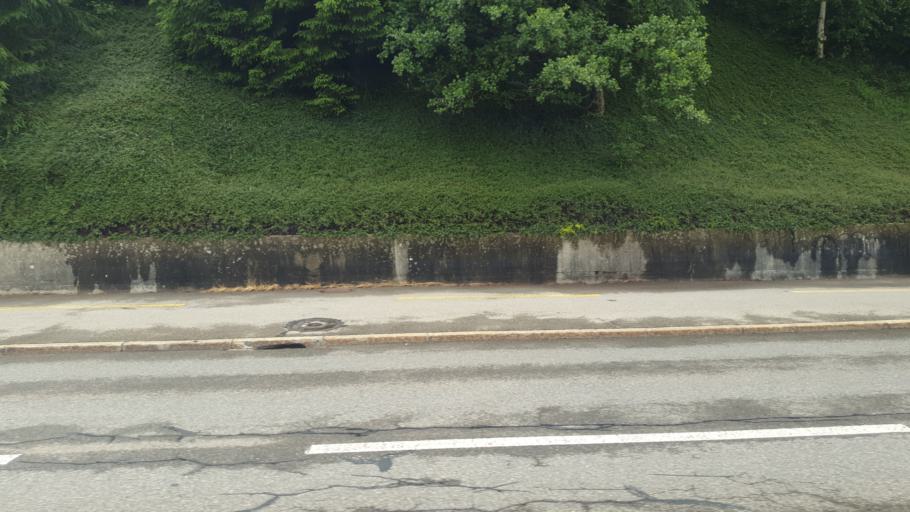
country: CH
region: Appenzell Ausserrhoden
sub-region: Bezirk Mittelland
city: Teufen
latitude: 47.3956
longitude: 9.3649
